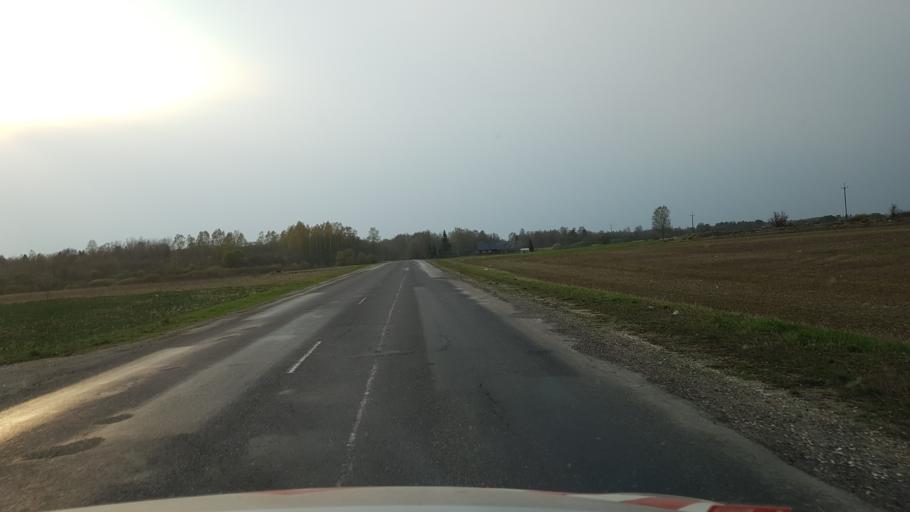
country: EE
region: Harju
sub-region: Raasiku vald
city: Raasiku
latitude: 59.3406
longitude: 25.1386
